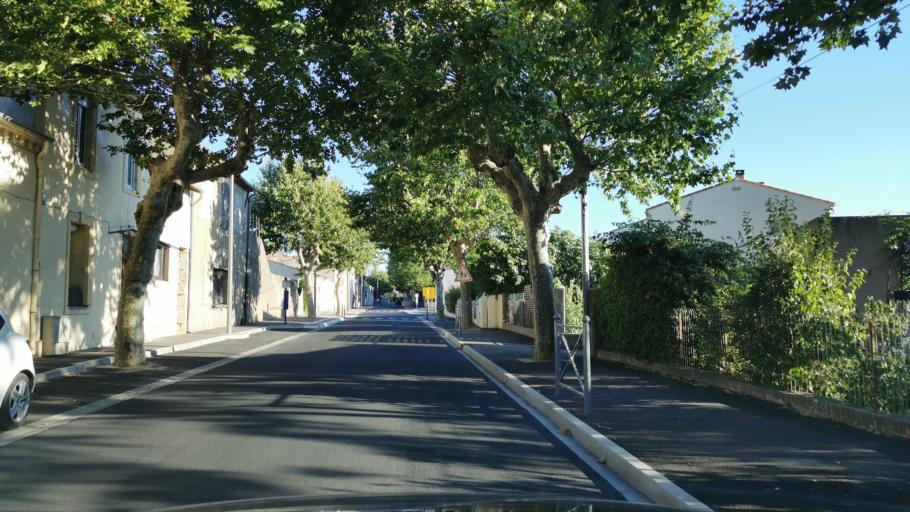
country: FR
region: Languedoc-Roussillon
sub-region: Departement de l'Aude
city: Ouveillan
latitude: 43.2475
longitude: 2.9972
